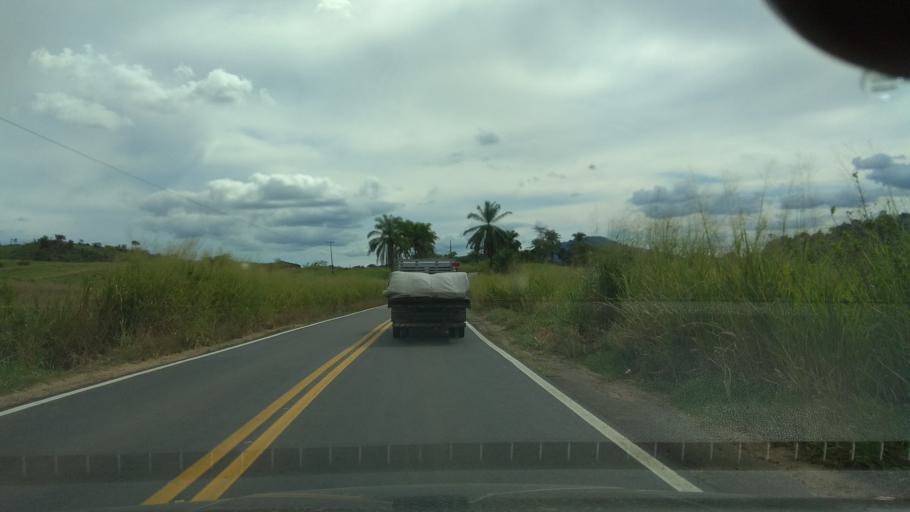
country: BR
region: Bahia
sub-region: Ipiau
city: Ipiau
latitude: -14.1937
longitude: -39.6494
